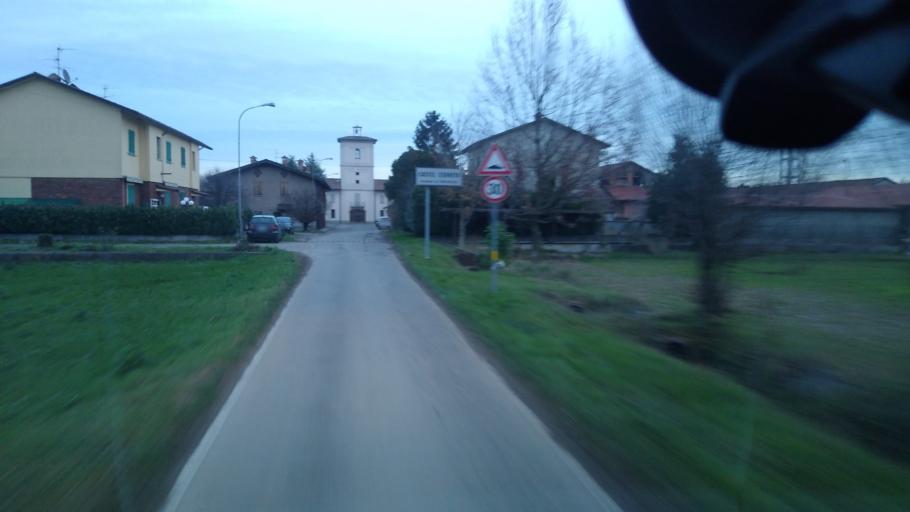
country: IT
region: Lombardy
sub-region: Provincia di Bergamo
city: Geromina
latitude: 45.5506
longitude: 9.5751
